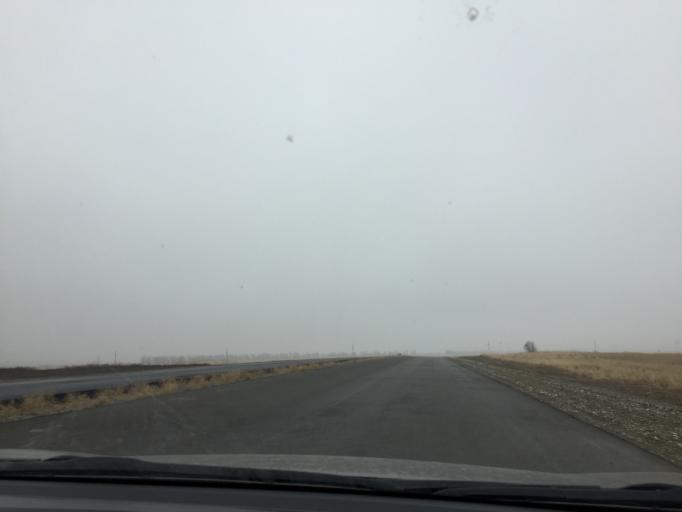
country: KZ
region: Ongtustik Qazaqstan
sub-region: Tulkibas Audany
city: Zhabagly
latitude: 42.5072
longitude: 70.4325
